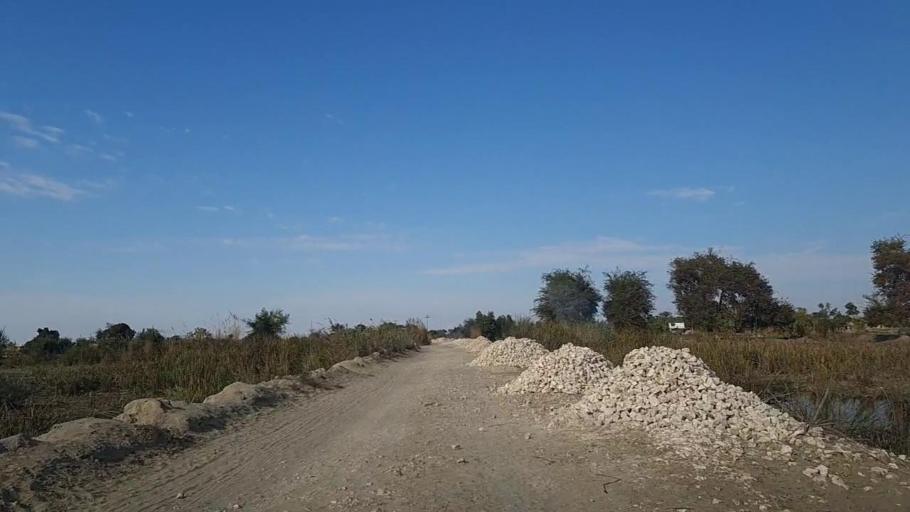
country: PK
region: Sindh
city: Khadro
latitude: 26.3043
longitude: 68.8141
